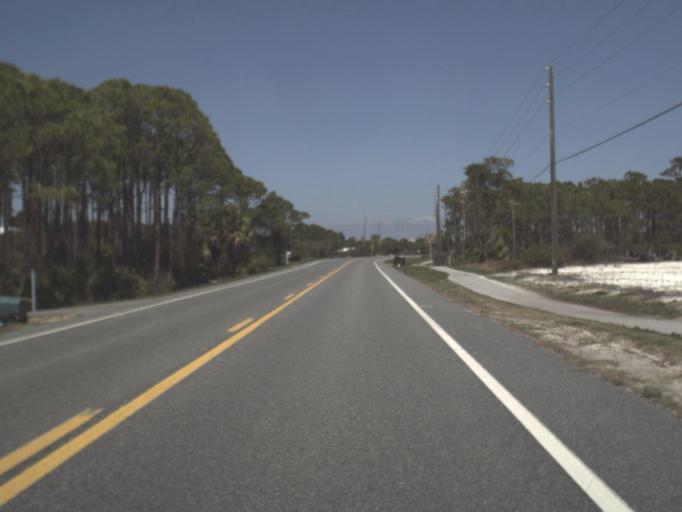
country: US
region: Florida
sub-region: Gulf County
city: Port Saint Joe
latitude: 29.7407
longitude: -85.3947
